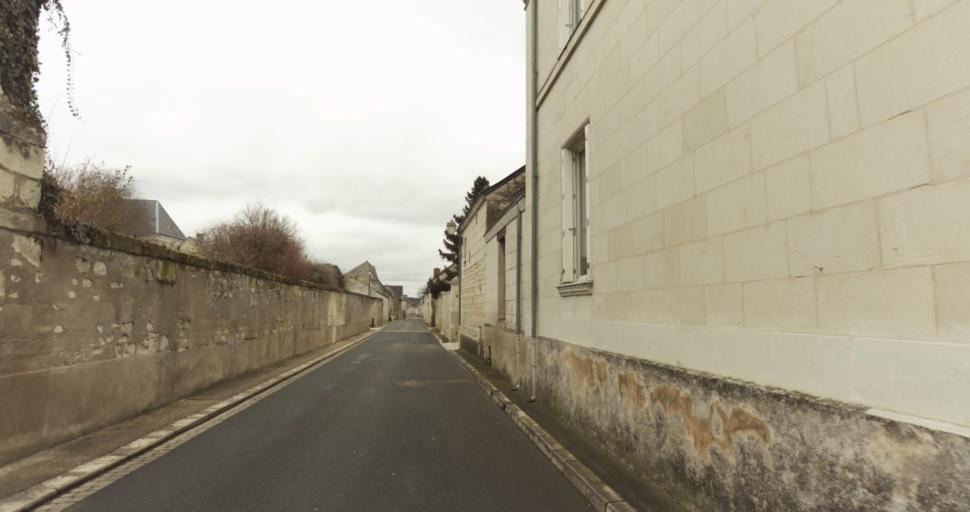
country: FR
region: Pays de la Loire
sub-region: Departement de Maine-et-Loire
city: Chace
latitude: 47.2145
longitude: -0.0735
